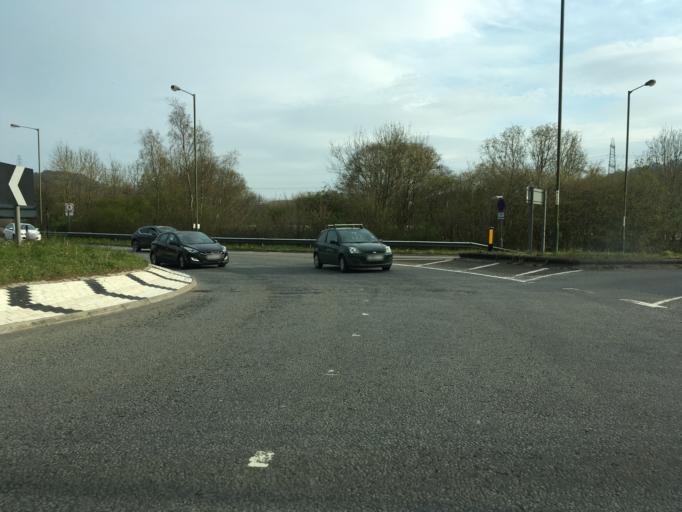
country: GB
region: Wales
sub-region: Caerphilly County Borough
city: Maesycwmmer
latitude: 51.6321
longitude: -3.2305
